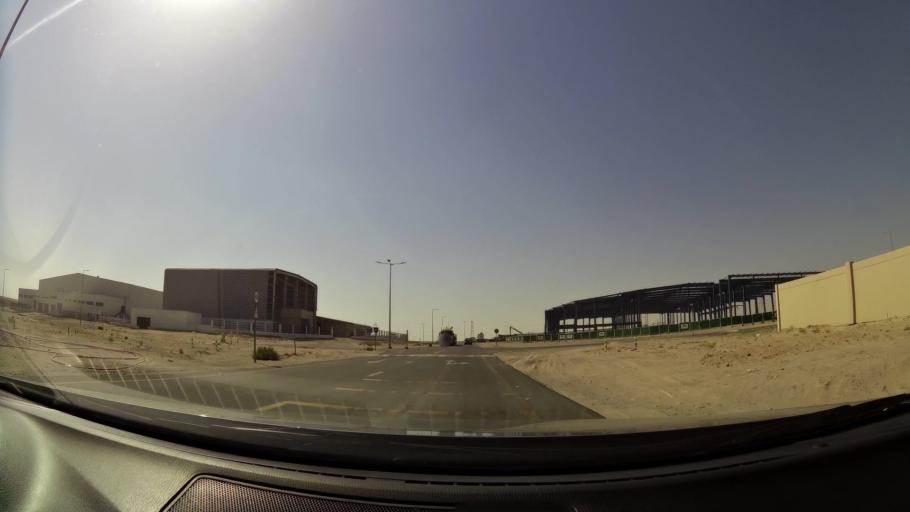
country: AE
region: Dubai
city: Dubai
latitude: 24.9133
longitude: 55.0701
